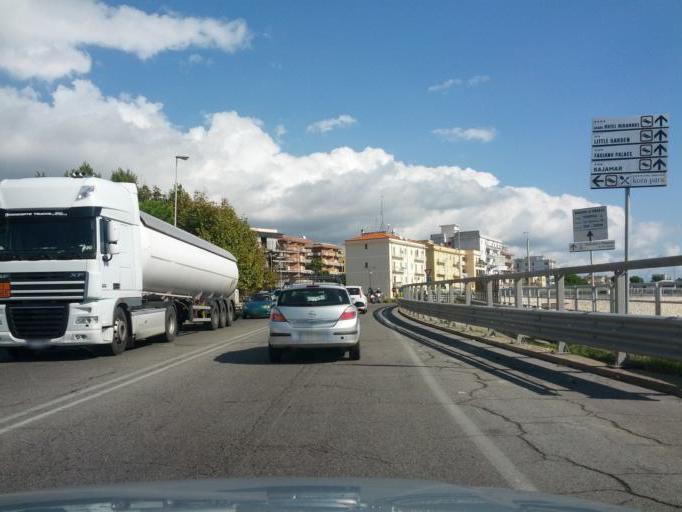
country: IT
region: Latium
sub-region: Provincia di Latina
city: Formia
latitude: 41.2602
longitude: 13.6181
